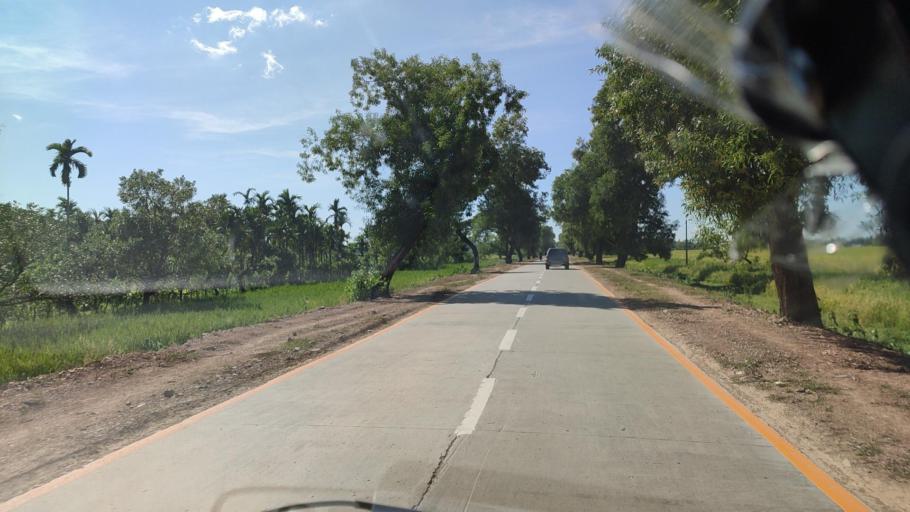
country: MM
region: Rakhine
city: Sittwe
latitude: 20.4785
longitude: 93.2764
